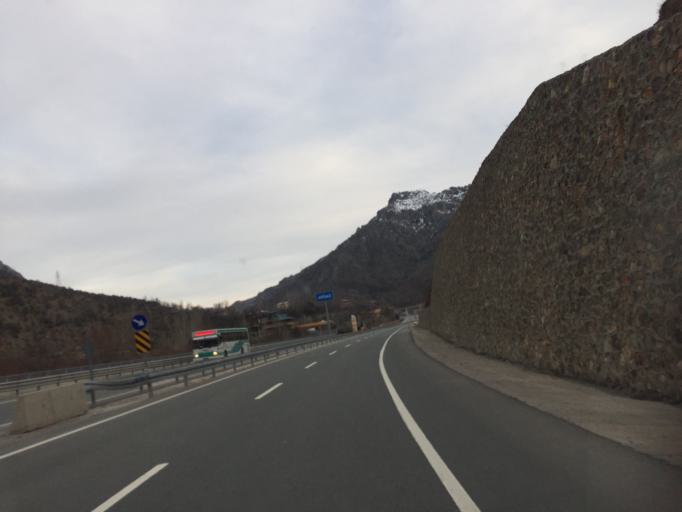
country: TR
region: Gumushane
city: Torul
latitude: 40.5457
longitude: 39.3233
